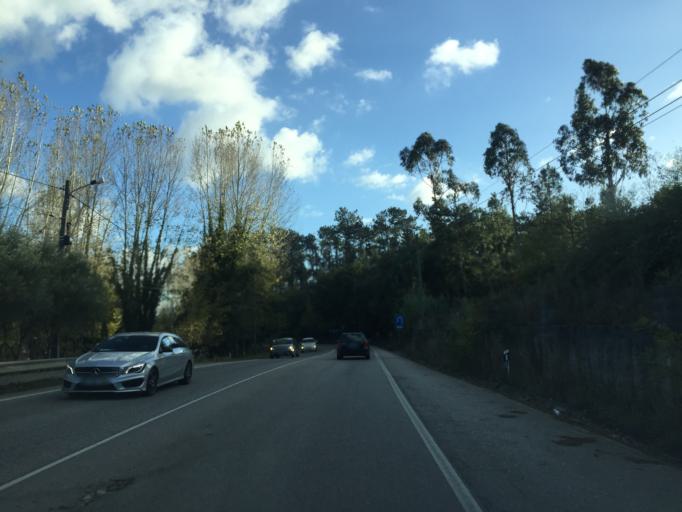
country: PT
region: Leiria
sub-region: Leiria
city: Souto da Carpalhosa
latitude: 39.8412
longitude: -8.8404
